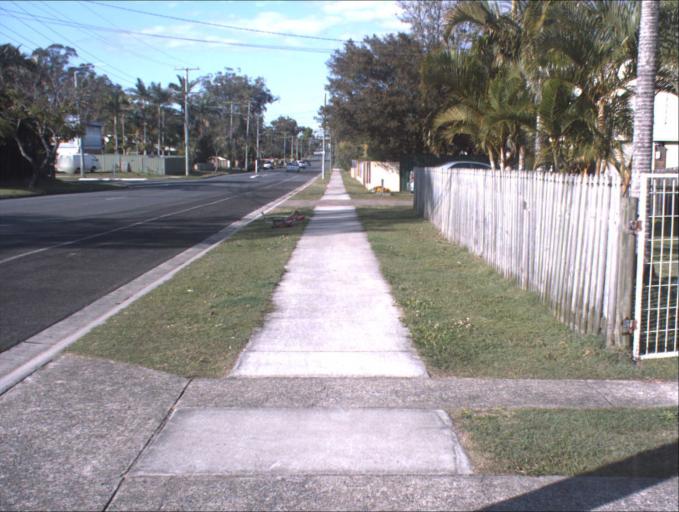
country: AU
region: Queensland
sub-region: Logan
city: Waterford West
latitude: -27.6753
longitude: 153.1009
